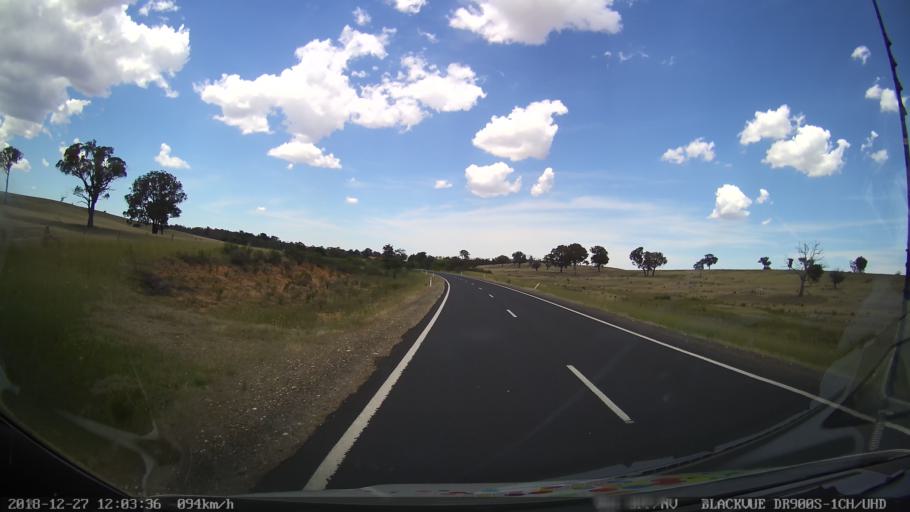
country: AU
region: New South Wales
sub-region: Blayney
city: Blayney
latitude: -33.7875
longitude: 149.3575
